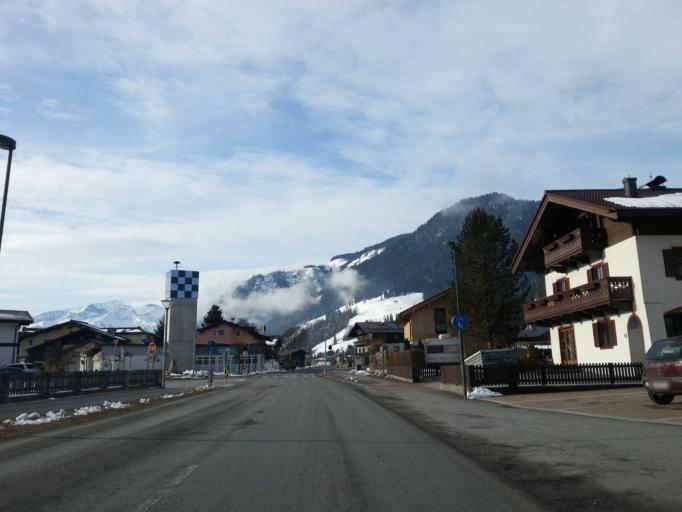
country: AT
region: Salzburg
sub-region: Politischer Bezirk Zell am See
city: Maishofen
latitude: 47.3693
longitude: 12.8055
